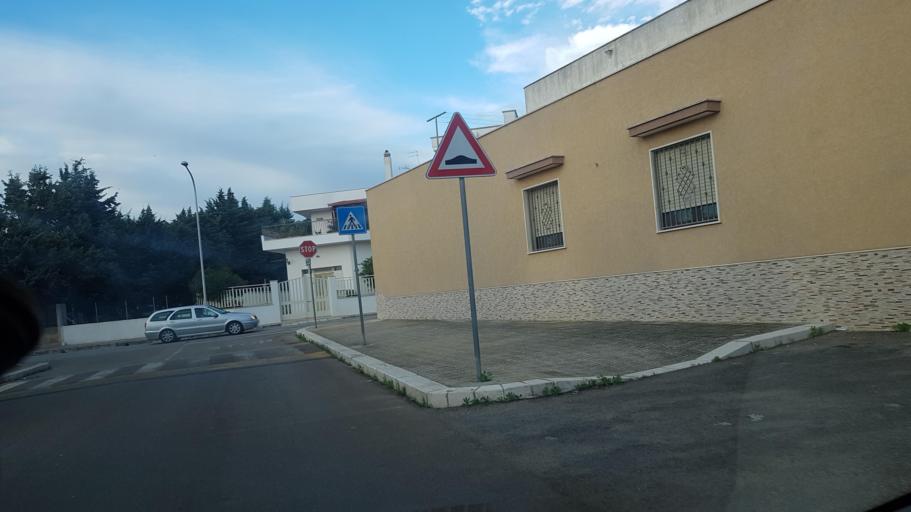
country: IT
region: Apulia
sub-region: Provincia di Brindisi
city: San Vito dei Normanni
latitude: 40.6597
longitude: 17.6993
